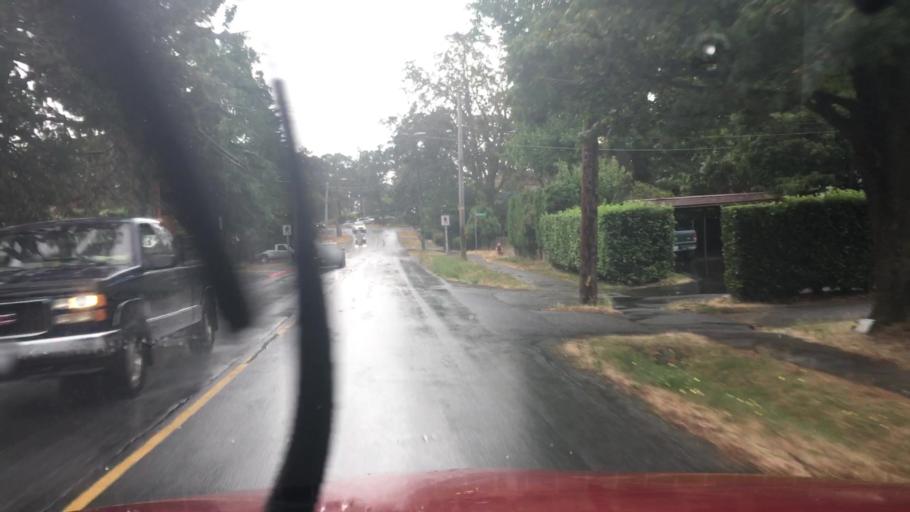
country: CA
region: British Columbia
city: Victoria
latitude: 48.4560
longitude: -123.3509
